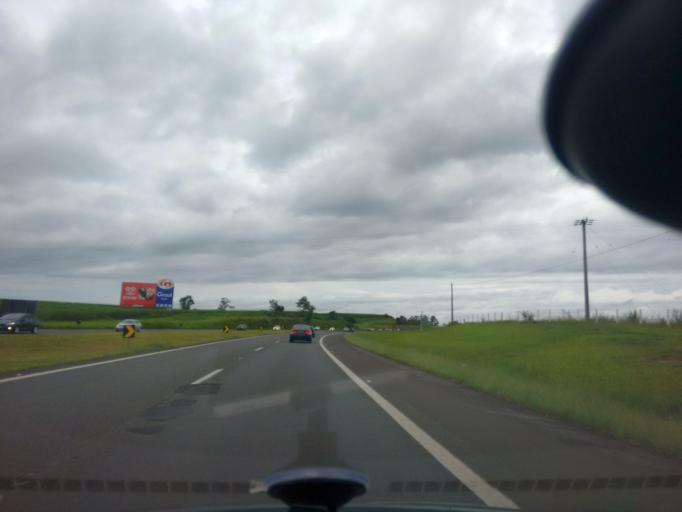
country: BR
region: Sao Paulo
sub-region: Rio Claro
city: Rio Claro
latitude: -22.3474
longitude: -47.6508
